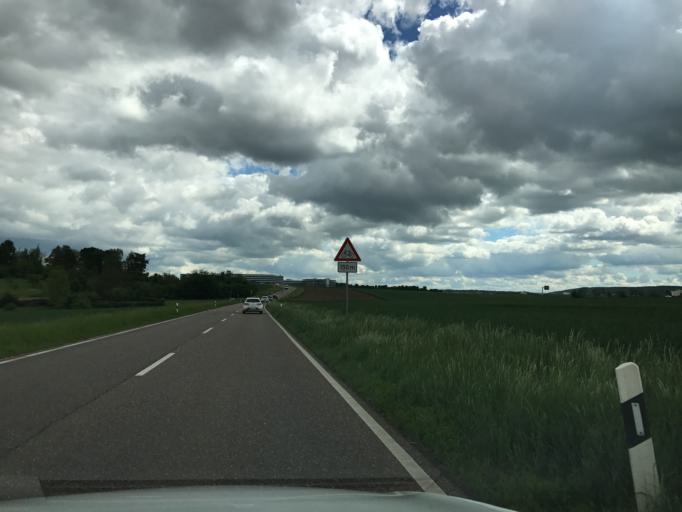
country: DE
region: Baden-Wuerttemberg
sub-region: Regierungsbezirk Stuttgart
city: Gerlingen
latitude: 48.8117
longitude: 9.0470
